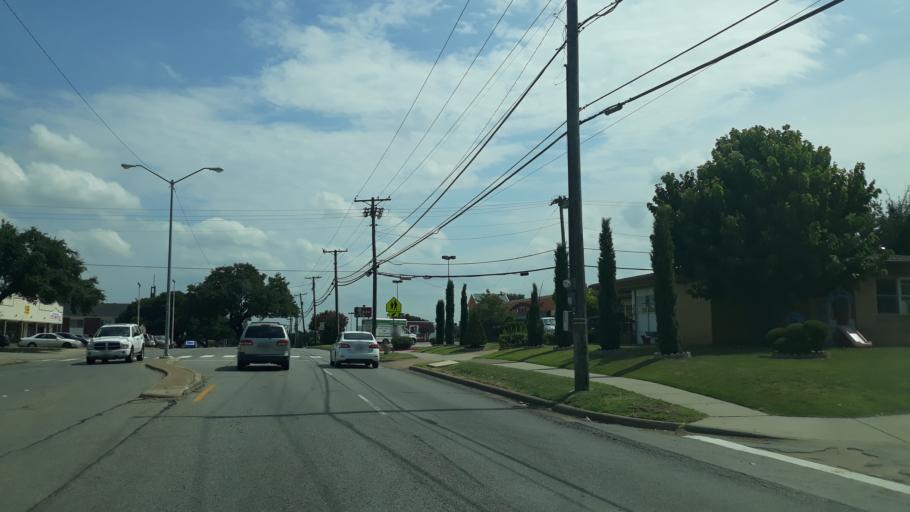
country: US
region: Texas
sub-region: Dallas County
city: Irving
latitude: 32.8335
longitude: -96.9765
